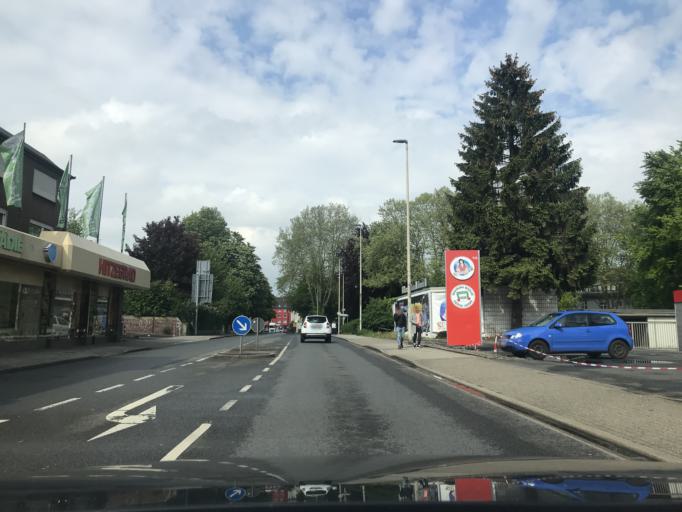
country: DE
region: North Rhine-Westphalia
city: Schwerte
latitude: 51.4431
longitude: 7.5621
